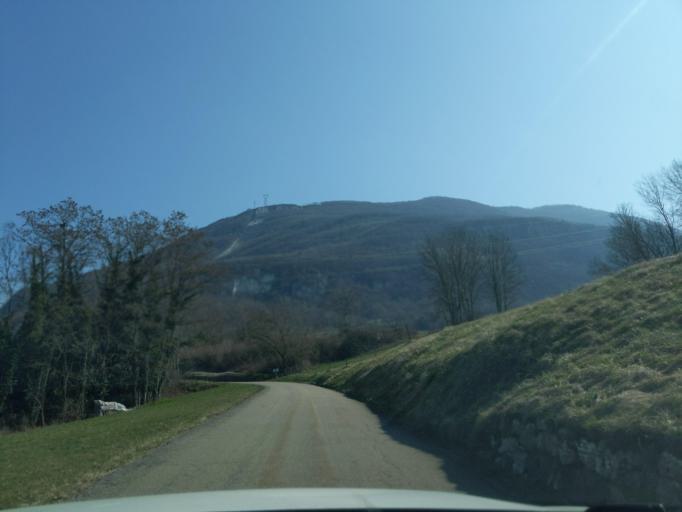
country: FR
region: Rhone-Alpes
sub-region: Departement de la Haute-Savoie
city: Versonnex
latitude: 45.9286
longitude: 5.8419
